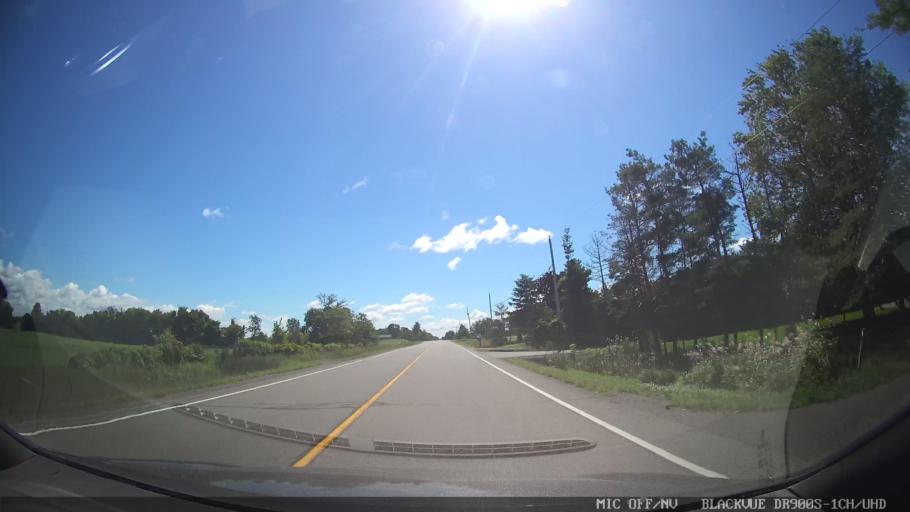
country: CA
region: Ontario
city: Bells Corners
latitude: 45.1781
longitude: -75.7740
